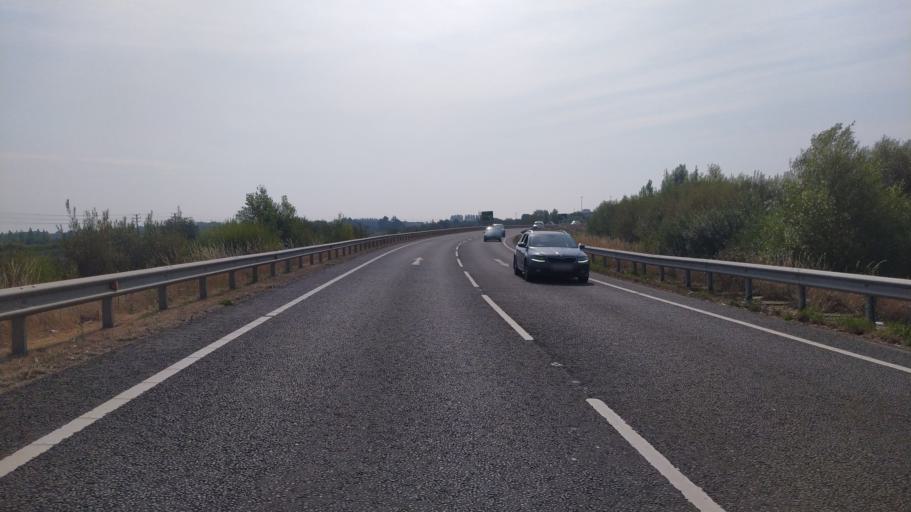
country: GB
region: England
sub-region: West Sussex
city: Bognor Regis
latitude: 50.8057
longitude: -0.6805
